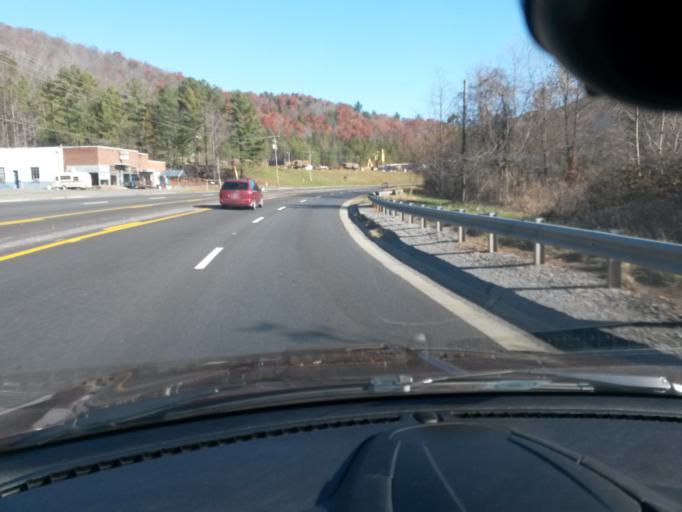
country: US
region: Virginia
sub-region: Patrick County
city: Stuart
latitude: 36.6543
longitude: -80.2831
